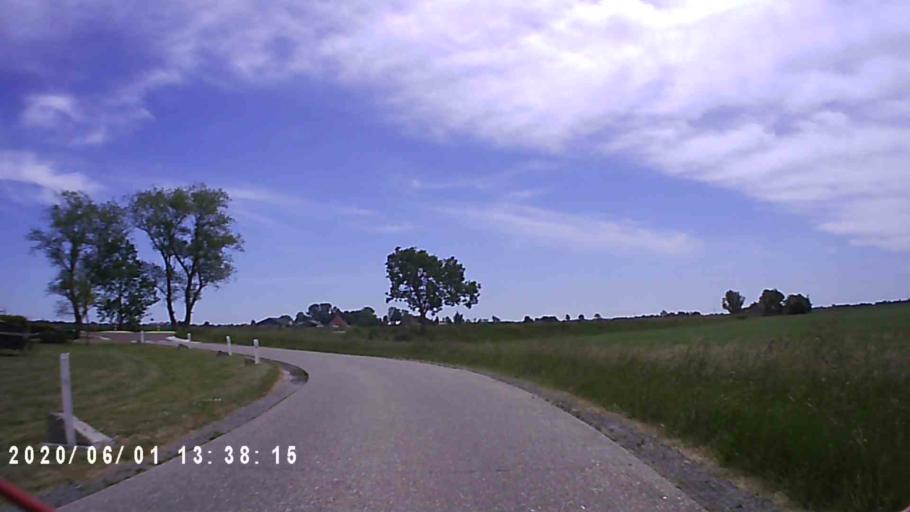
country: NL
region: Friesland
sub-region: Gemeente Littenseradiel
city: Wommels
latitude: 53.0846
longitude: 5.5966
